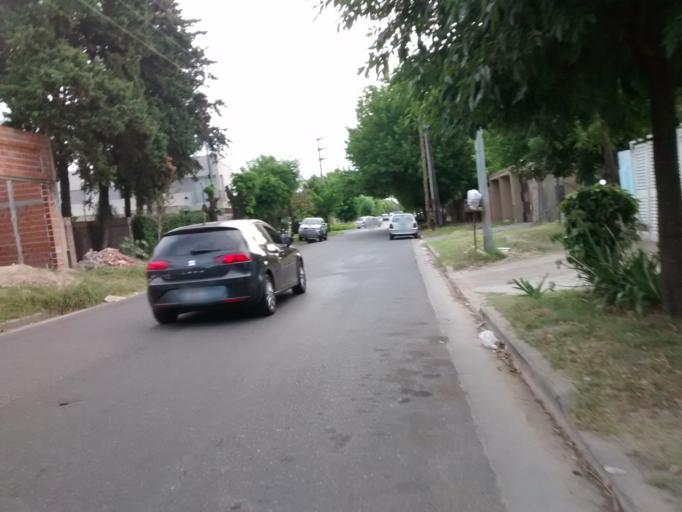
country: AR
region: Buenos Aires
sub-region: Partido de La Plata
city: La Plata
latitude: -34.8730
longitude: -58.0587
